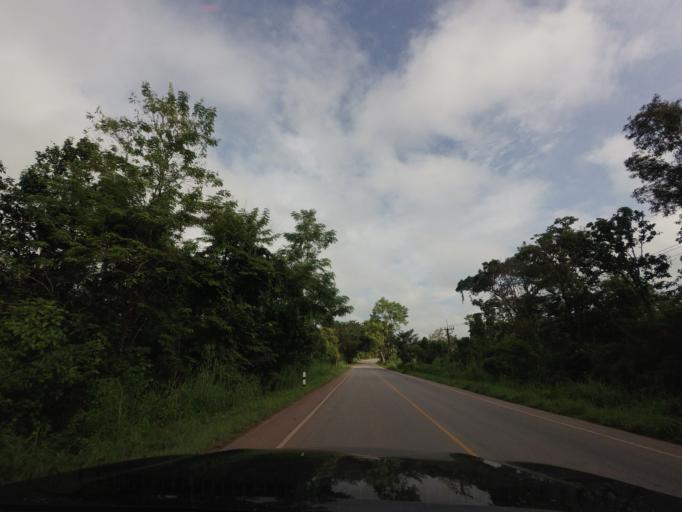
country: TH
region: Changwat Udon Thani
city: Nam Som
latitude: 17.8412
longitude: 102.2564
